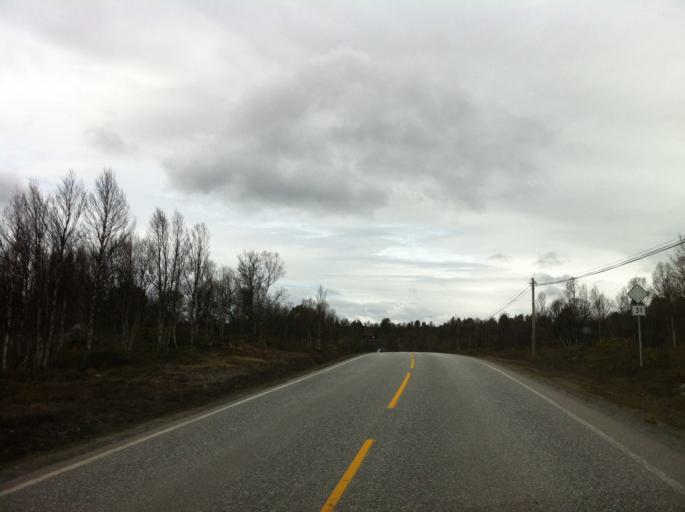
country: NO
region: Sor-Trondelag
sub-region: Roros
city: Roros
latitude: 62.5990
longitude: 11.4775
